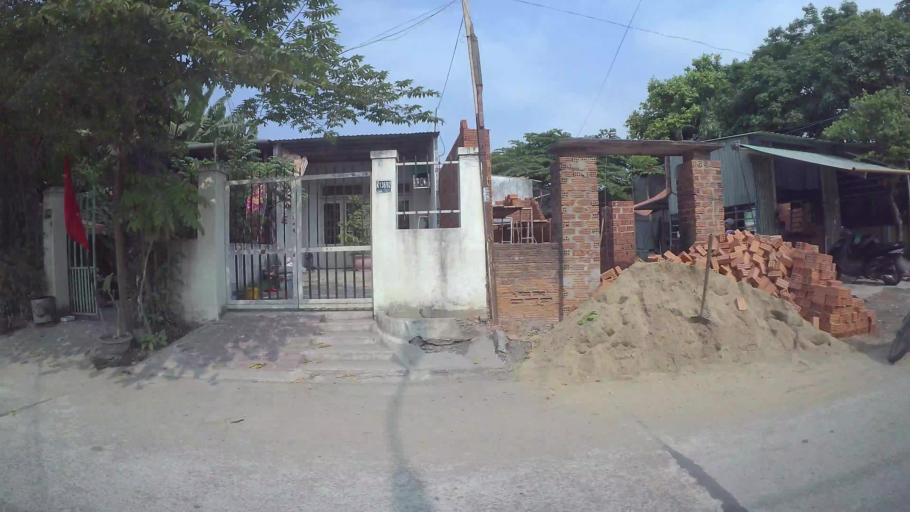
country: VN
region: Da Nang
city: Lien Chieu
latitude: 16.0574
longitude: 108.1567
